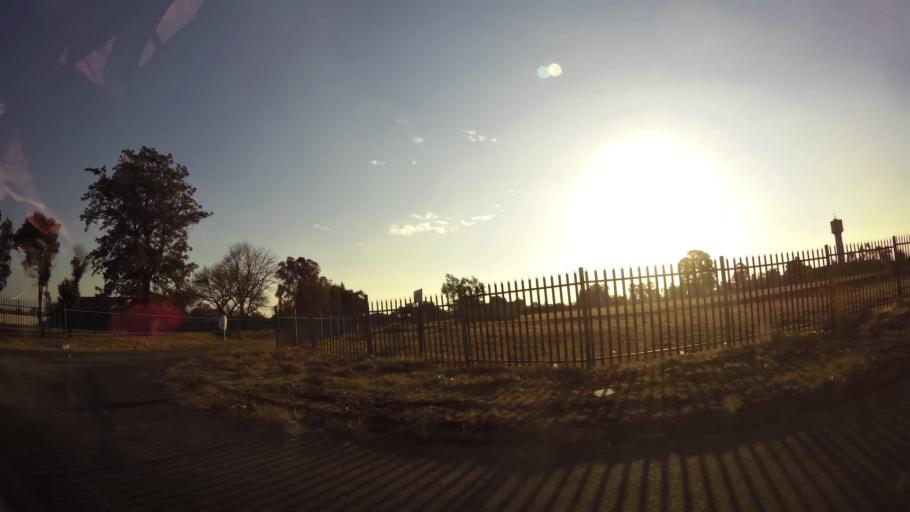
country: ZA
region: Gauteng
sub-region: West Rand District Municipality
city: Randfontein
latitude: -26.2040
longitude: 27.6490
